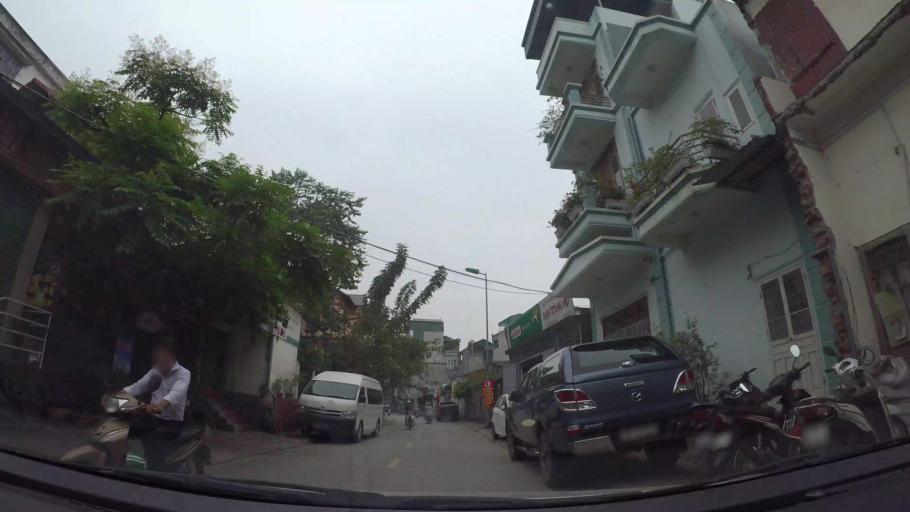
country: VN
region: Ha Noi
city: Dong Da
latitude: 21.0383
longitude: 105.8235
